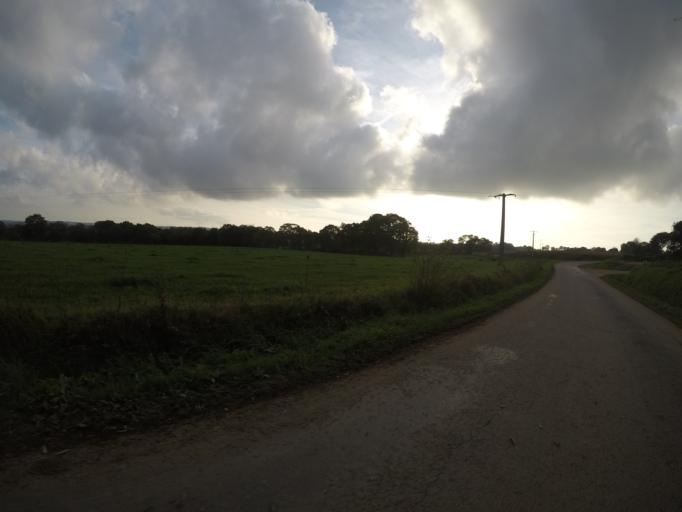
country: FR
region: Brittany
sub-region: Departement des Cotes-d'Armor
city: Bourbriac
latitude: 48.5082
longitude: -3.2631
